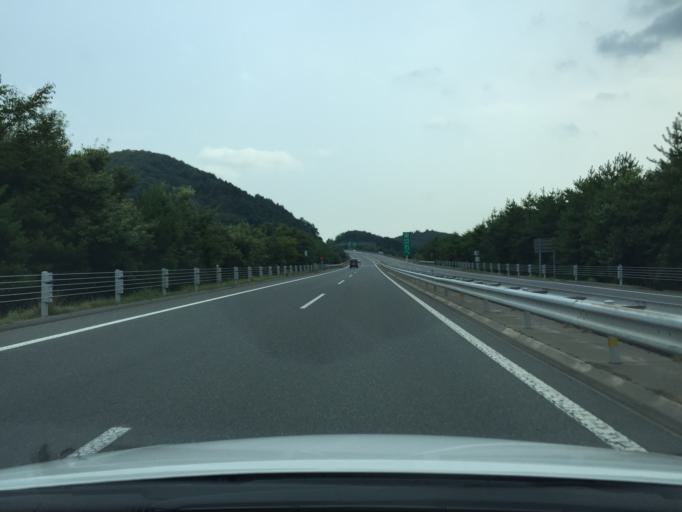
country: JP
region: Fukushima
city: Iwaki
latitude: 37.0495
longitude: 140.8055
